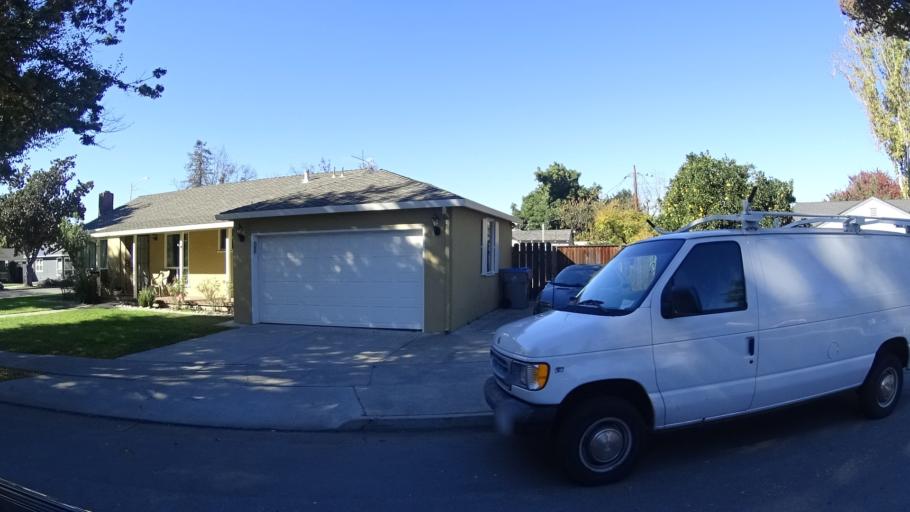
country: US
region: California
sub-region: Santa Clara County
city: San Jose
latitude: 37.3581
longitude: -121.9086
